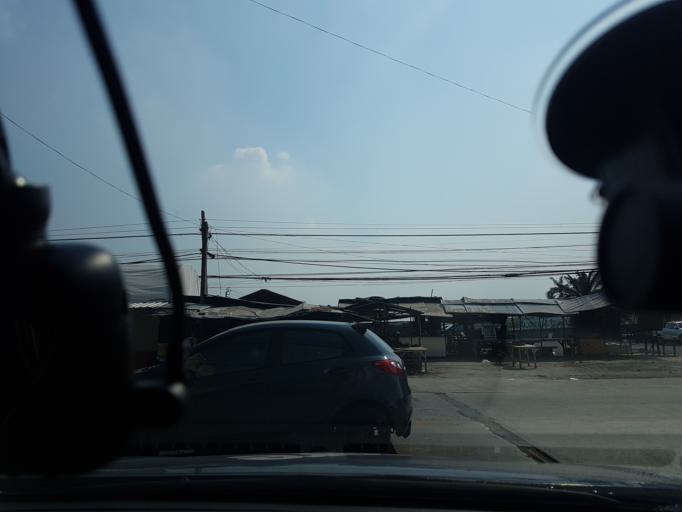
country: TH
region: Bangkok
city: Khan Na Yao
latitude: 13.8411
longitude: 100.6980
